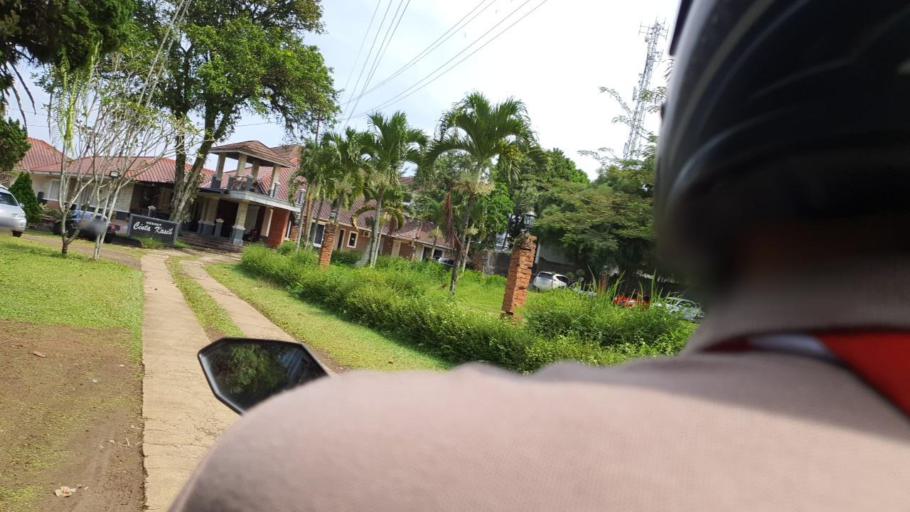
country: ID
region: West Java
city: Caringin
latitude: -6.6515
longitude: 106.9034
